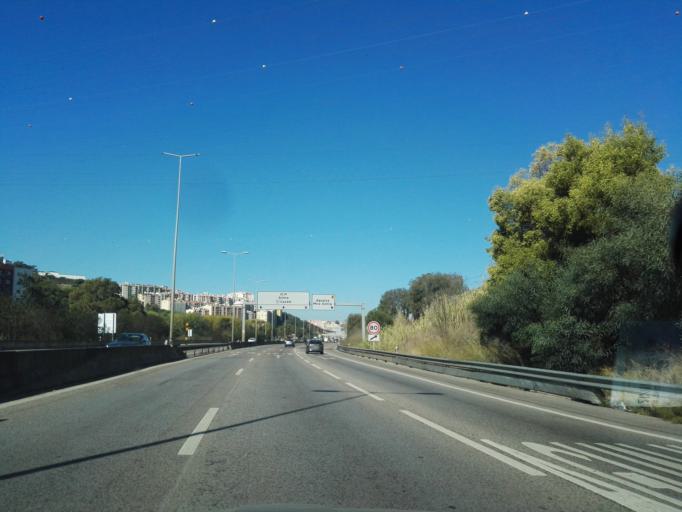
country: PT
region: Lisbon
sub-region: Sintra
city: Cacem
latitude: 38.7577
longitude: -9.2921
